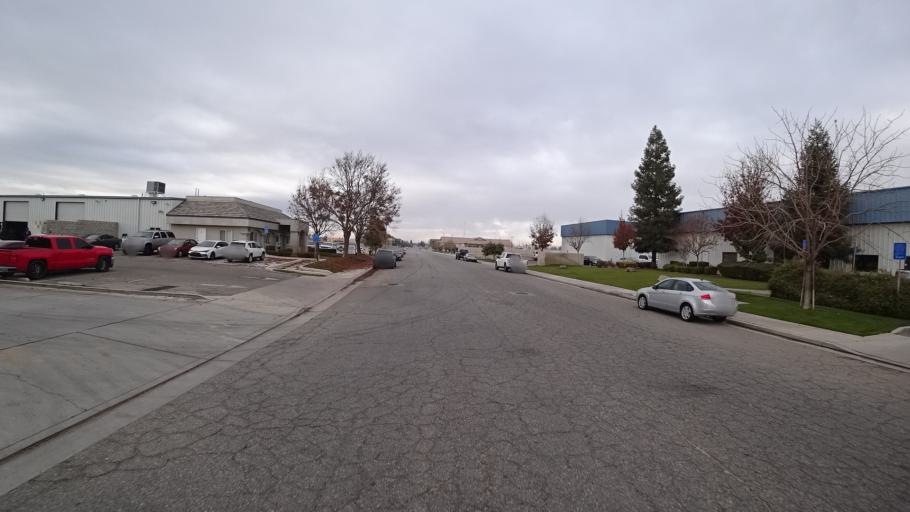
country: US
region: California
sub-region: Kern County
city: Greenfield
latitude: 35.3083
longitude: -119.0633
